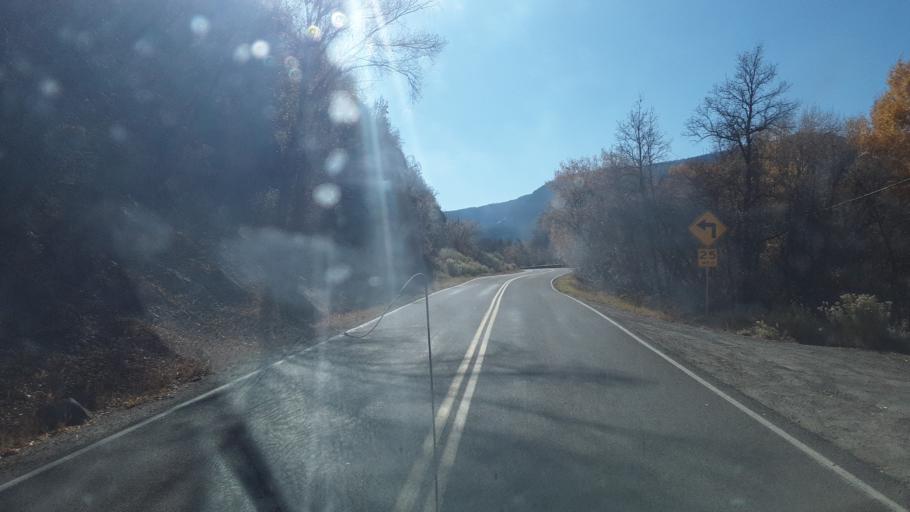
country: US
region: Colorado
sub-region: La Plata County
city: Durango
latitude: 37.3915
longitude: -107.8249
